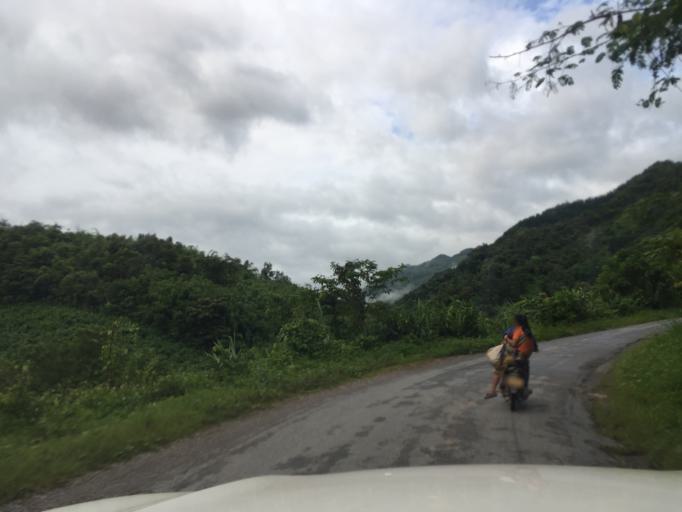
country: LA
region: Oudomxai
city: Muang La
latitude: 21.0360
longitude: 102.2394
